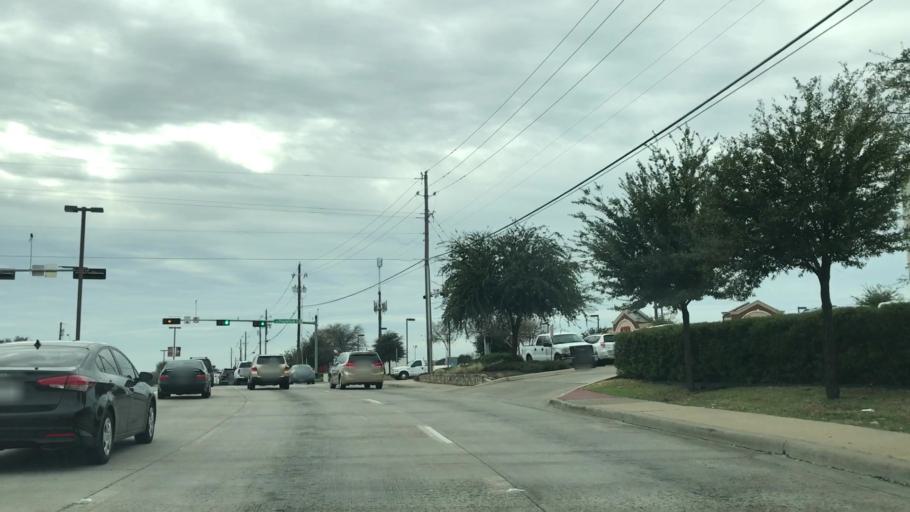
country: US
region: Texas
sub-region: Dallas County
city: Carrollton
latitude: 33.0009
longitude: -96.8867
